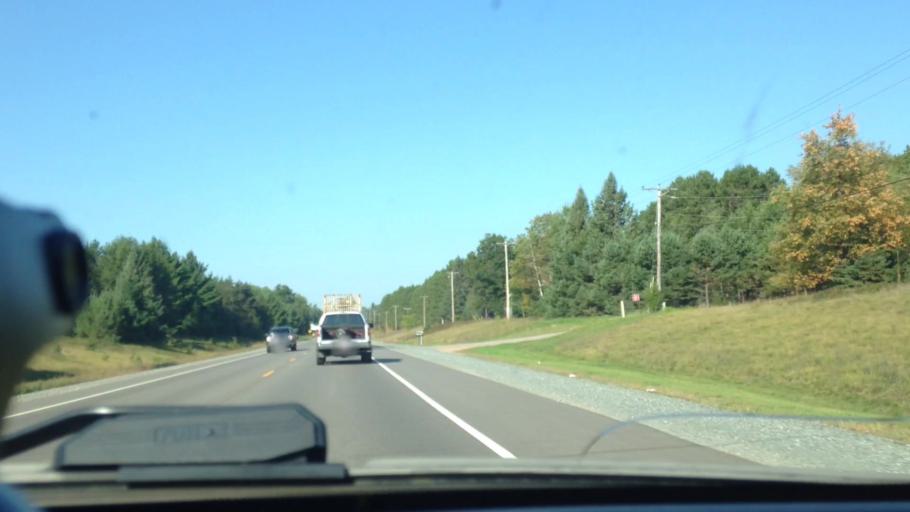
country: US
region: Michigan
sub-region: Dickinson County
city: Iron Mountain
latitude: 45.8760
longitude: -88.0989
